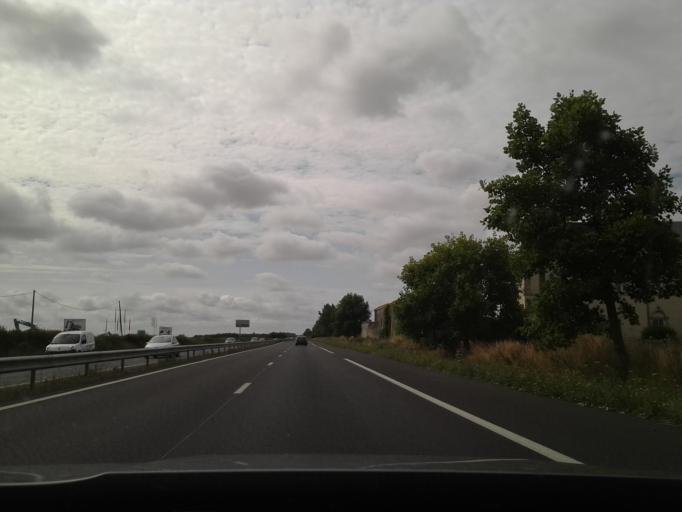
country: FR
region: Lower Normandy
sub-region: Departement du Calvados
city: Bretteville-sur-Laize
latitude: 49.0663
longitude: -0.2934
